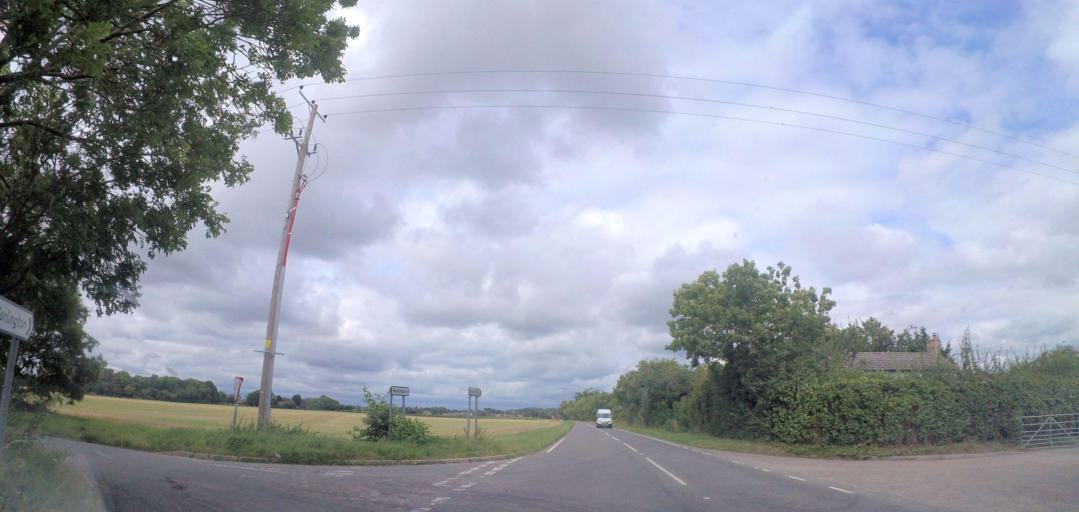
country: GB
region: England
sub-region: Suffolk
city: Lakenheath
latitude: 52.3264
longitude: 0.5109
